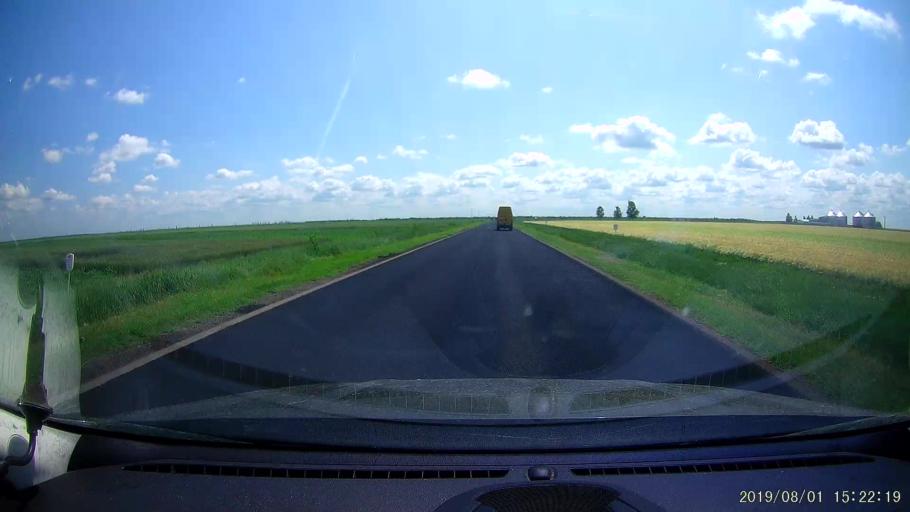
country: RO
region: Braila
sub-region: Comuna Viziru
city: Lanurile
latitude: 45.0554
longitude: 27.7783
